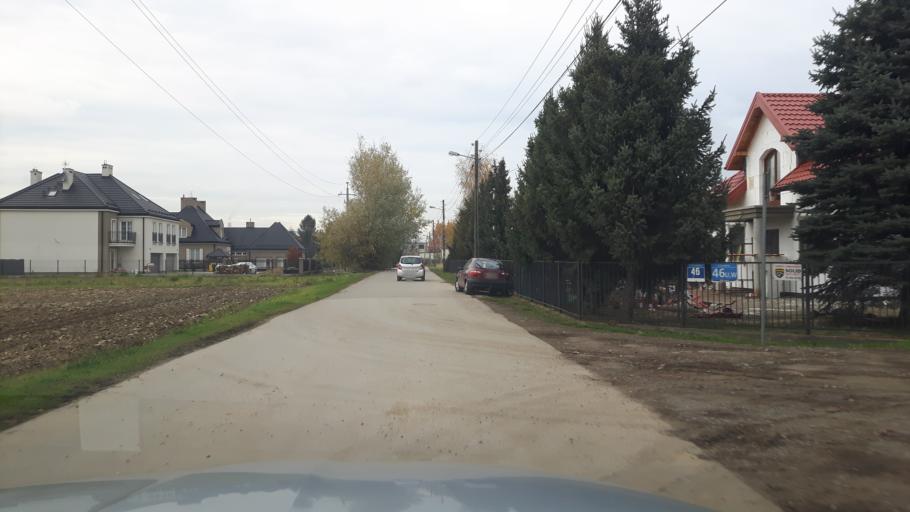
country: PL
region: Masovian Voivodeship
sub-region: Warszawa
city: Wilanow
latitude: 52.1597
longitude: 21.1264
